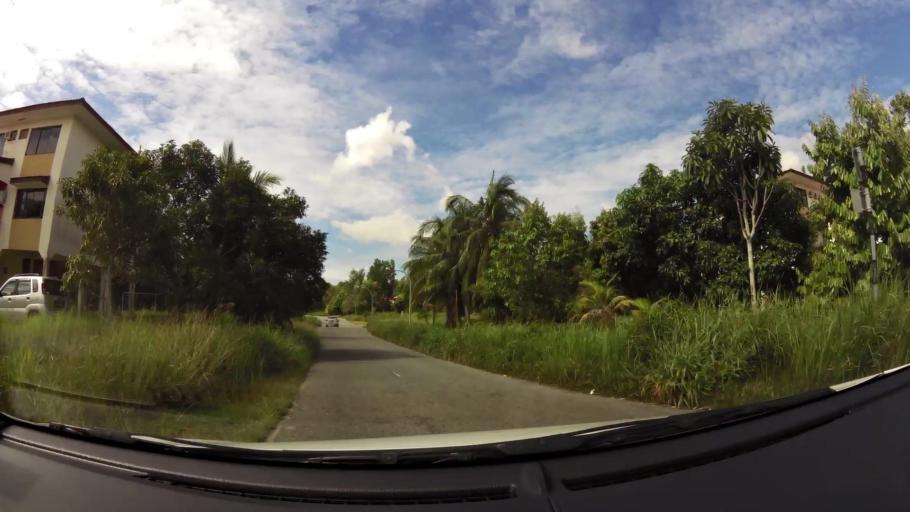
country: BN
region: Brunei and Muara
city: Bandar Seri Begawan
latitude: 4.9324
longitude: 114.9091
